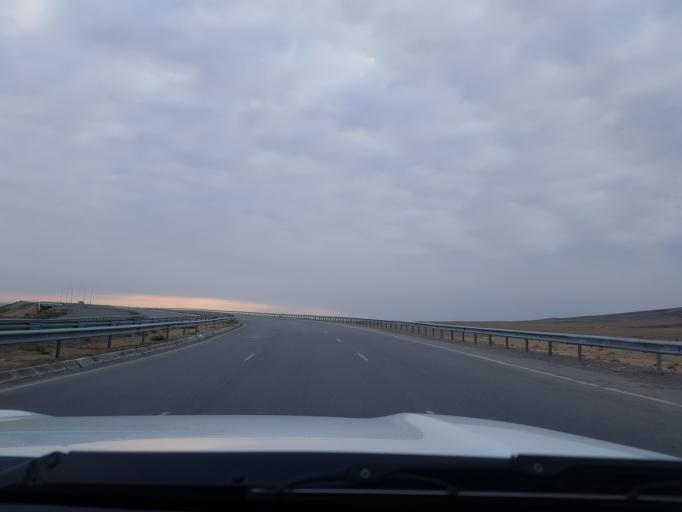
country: IR
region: Razavi Khorasan
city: Dargaz
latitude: 37.6820
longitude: 59.0739
